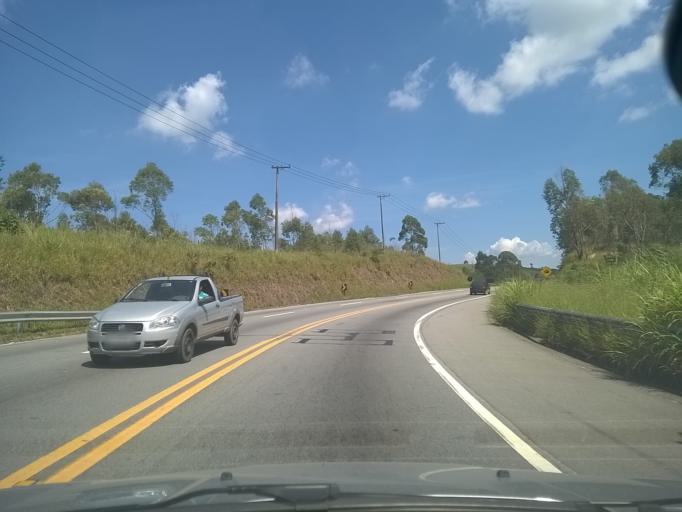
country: BR
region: Sao Paulo
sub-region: Francisco Morato
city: Francisco Morato
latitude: -23.2984
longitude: -46.7811
